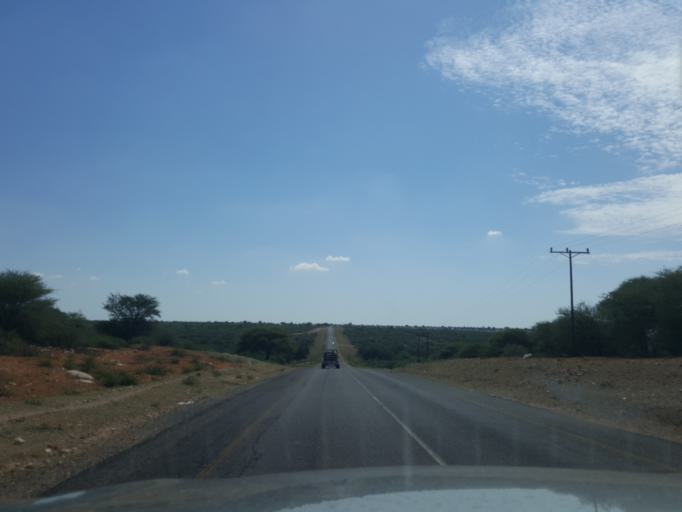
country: BW
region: Kweneng
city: Letlhakeng
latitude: -24.1190
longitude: 25.0618
